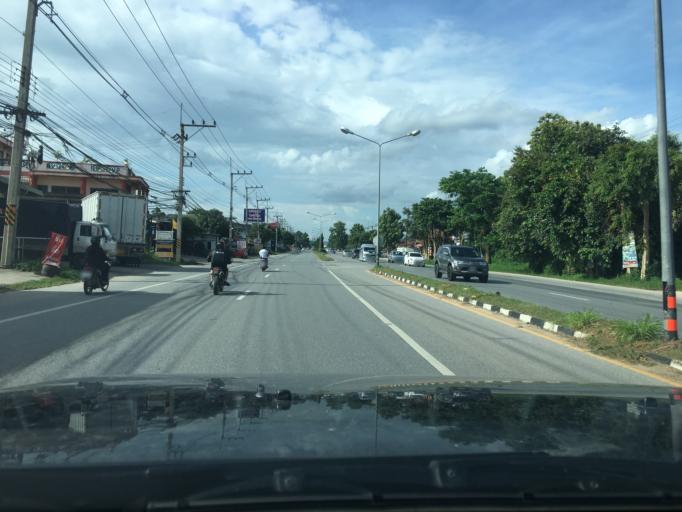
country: TH
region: Chiang Rai
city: Chiang Rai
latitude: 19.9498
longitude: 99.8486
